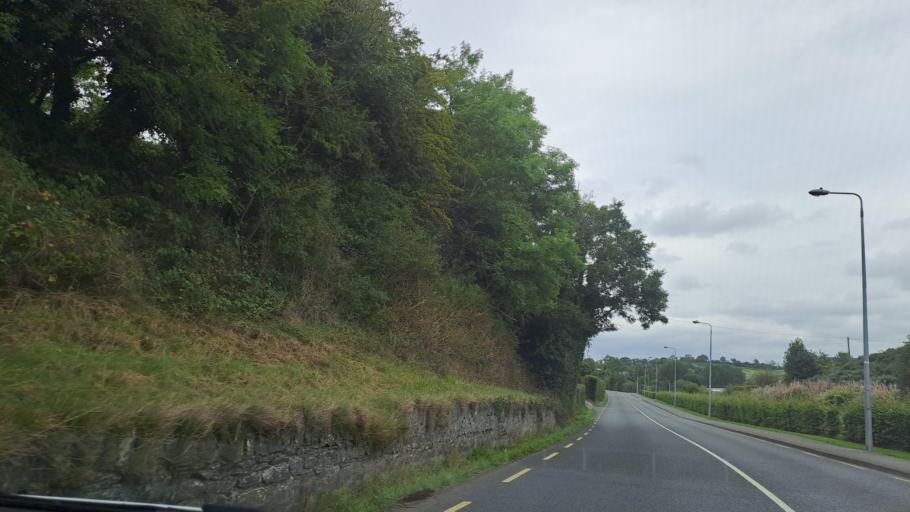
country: IE
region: Ulster
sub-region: An Cabhan
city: Bailieborough
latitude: 53.9221
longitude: -6.9702
